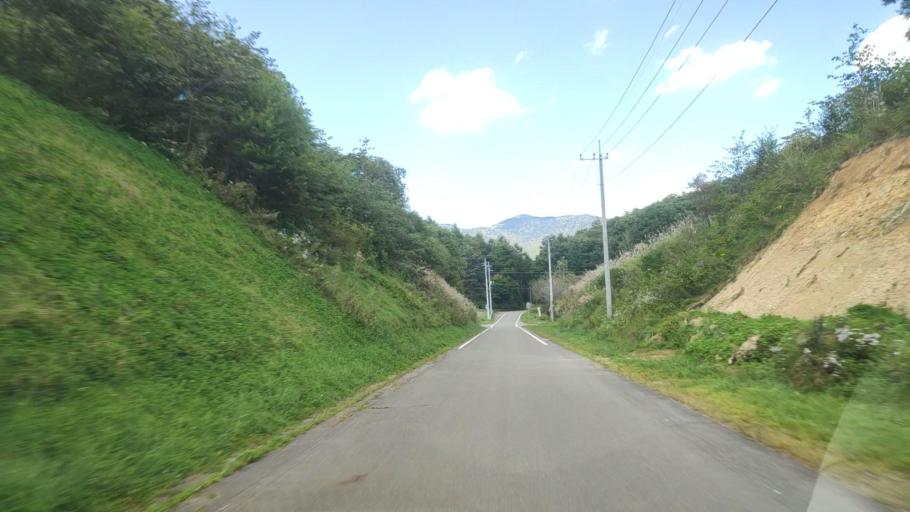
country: JP
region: Gunma
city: Nakanojomachi
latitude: 36.6456
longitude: 138.6201
